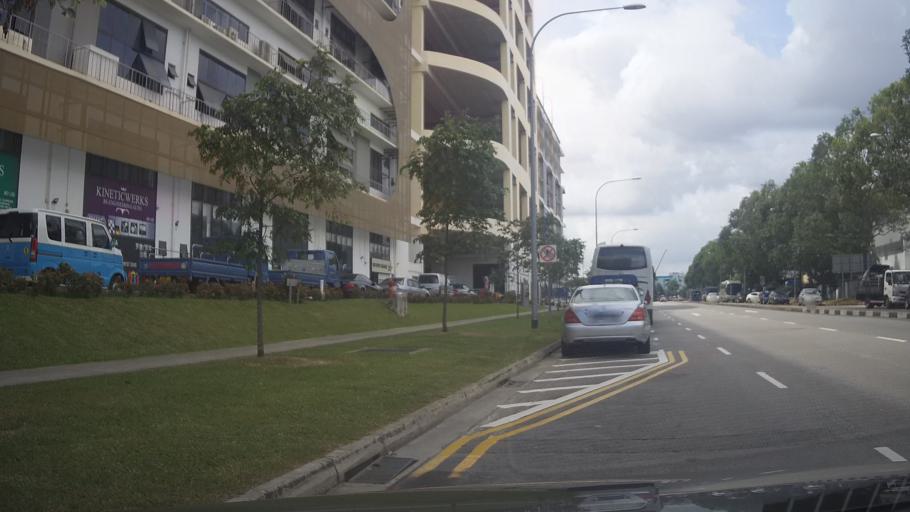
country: MY
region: Johor
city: Johor Bahru
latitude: 1.4499
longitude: 103.7988
